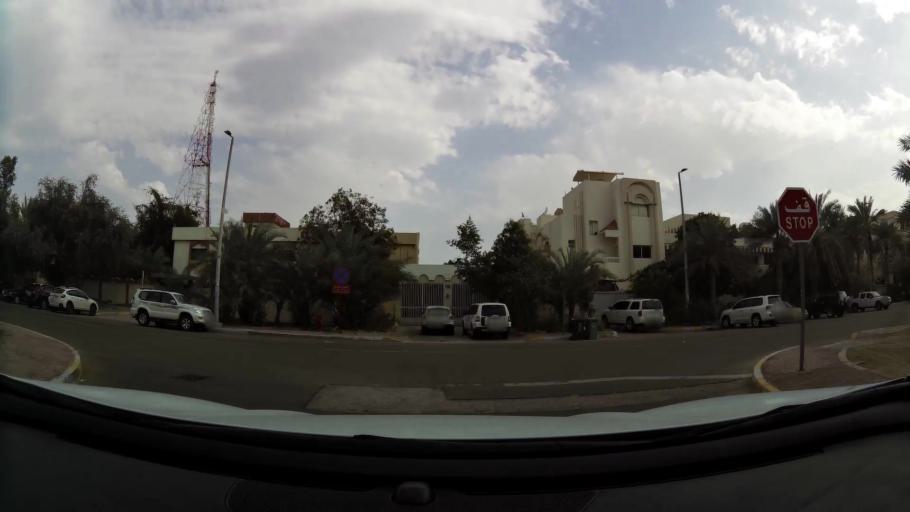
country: AE
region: Abu Dhabi
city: Abu Dhabi
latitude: 24.4608
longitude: 54.3529
